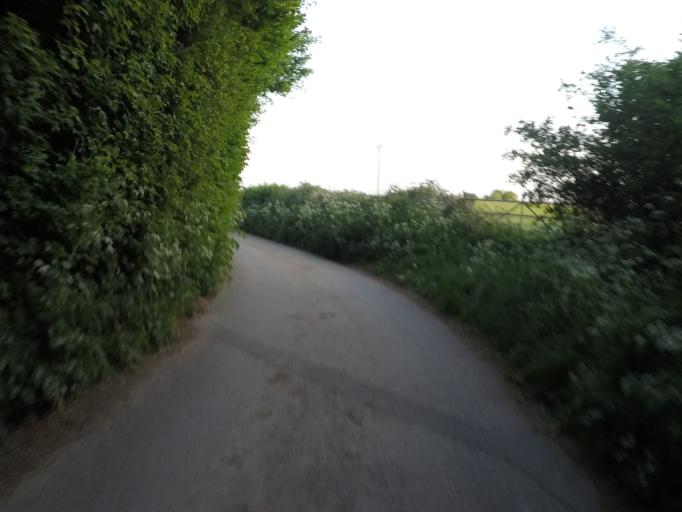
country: GB
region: England
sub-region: Oxfordshire
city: Charlbury
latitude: 51.8352
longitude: -1.5282
